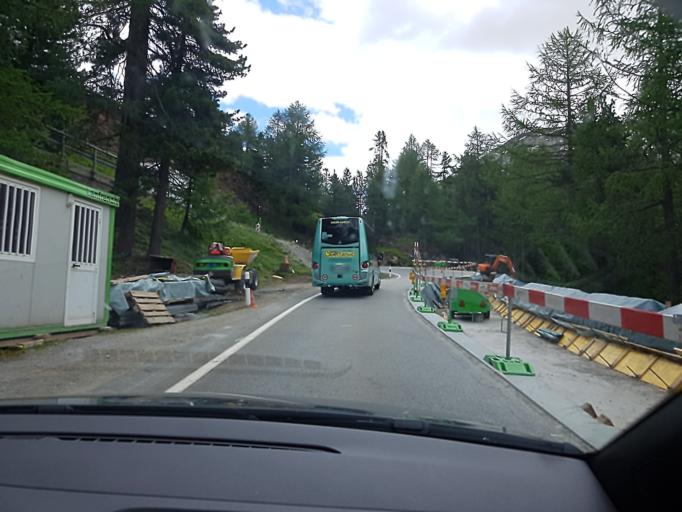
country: CH
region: Grisons
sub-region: Maloja District
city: Pontresina
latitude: 46.4572
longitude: 9.9419
